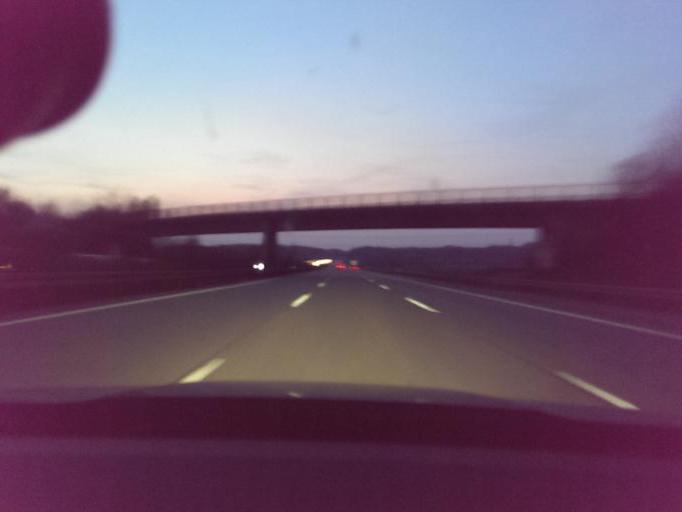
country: DE
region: Lower Saxony
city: Sarstedt
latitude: 52.2927
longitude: 9.8945
